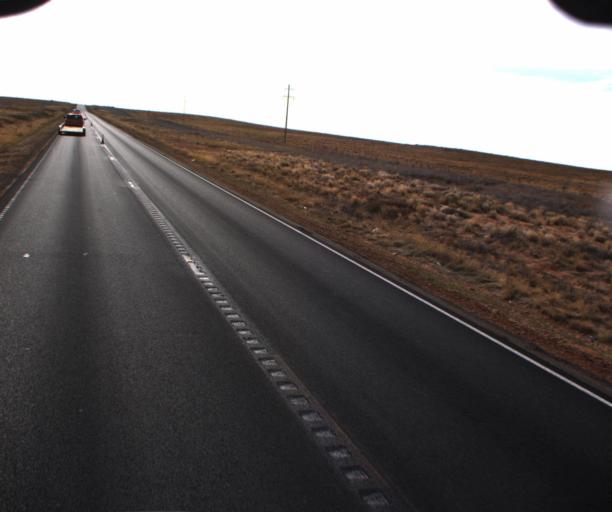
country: US
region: Arizona
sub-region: Apache County
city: Chinle
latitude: 36.0773
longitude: -109.6146
